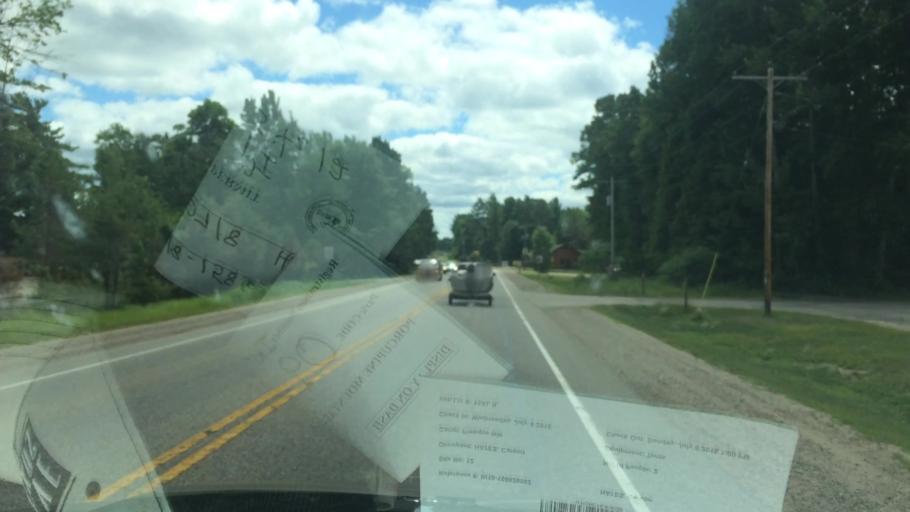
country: US
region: Wisconsin
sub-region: Vilas County
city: Eagle River
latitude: 45.8026
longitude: -89.3200
